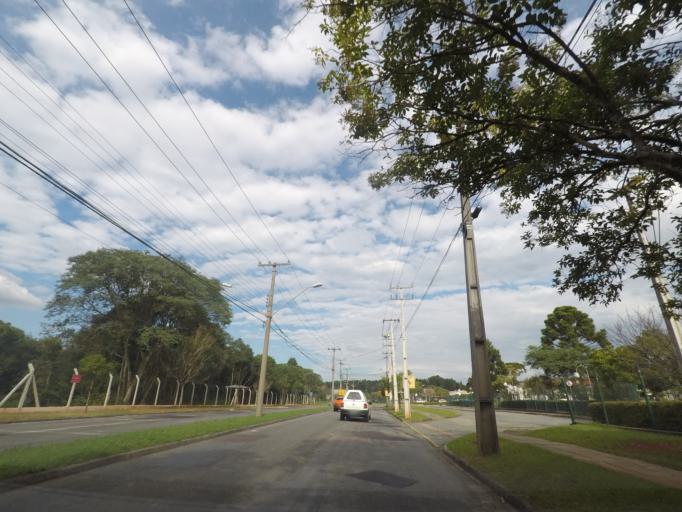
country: BR
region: Parana
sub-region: Sao Jose Dos Pinhais
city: Sao Jose dos Pinhais
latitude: -25.5325
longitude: -49.3084
